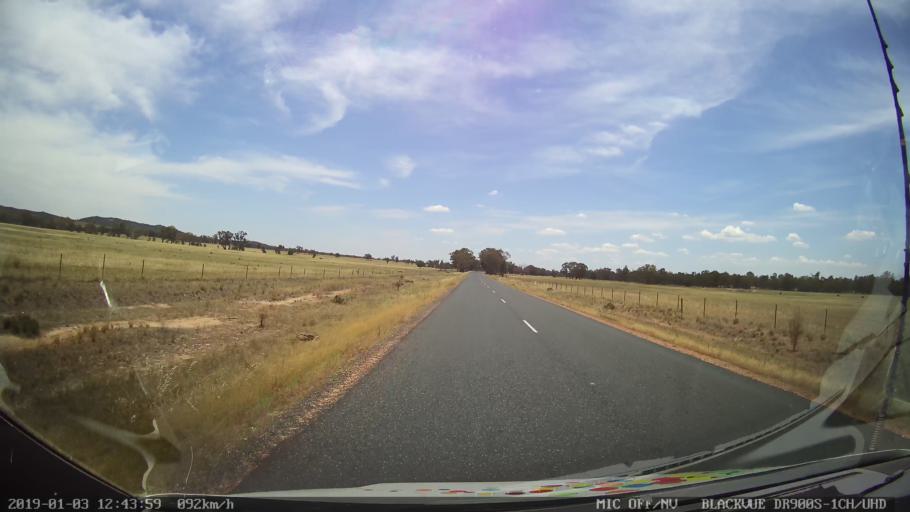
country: AU
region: New South Wales
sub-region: Weddin
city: Grenfell
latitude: -33.7677
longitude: 148.2147
